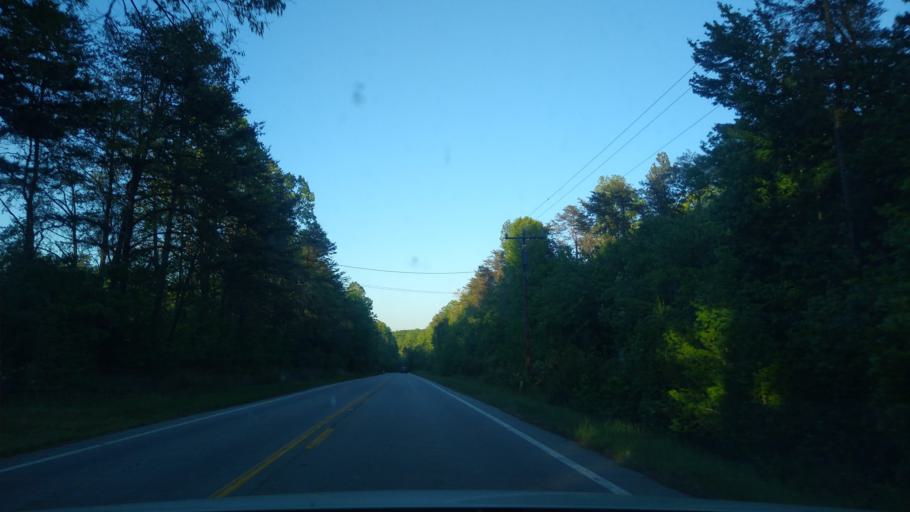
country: US
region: North Carolina
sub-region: Rockingham County
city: Reidsville
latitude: 36.3969
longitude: -79.5406
